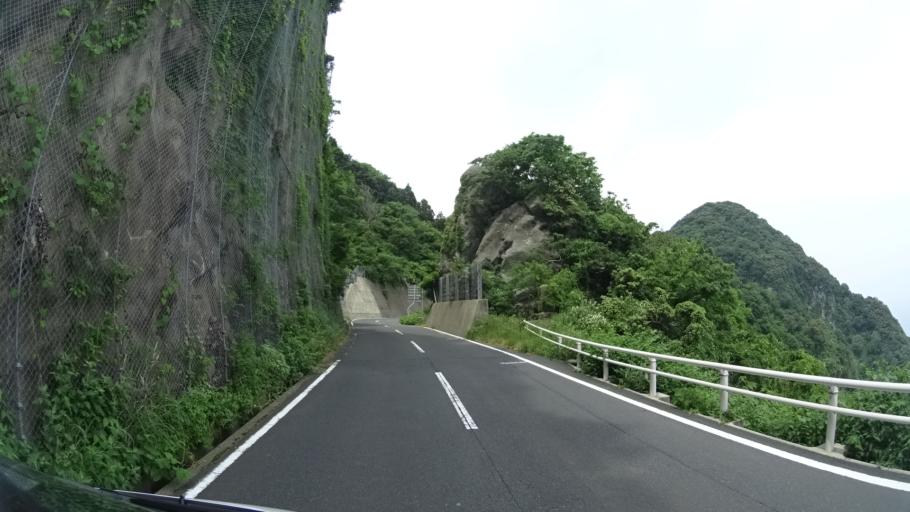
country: JP
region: Kyoto
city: Miyazu
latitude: 35.7678
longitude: 135.2330
